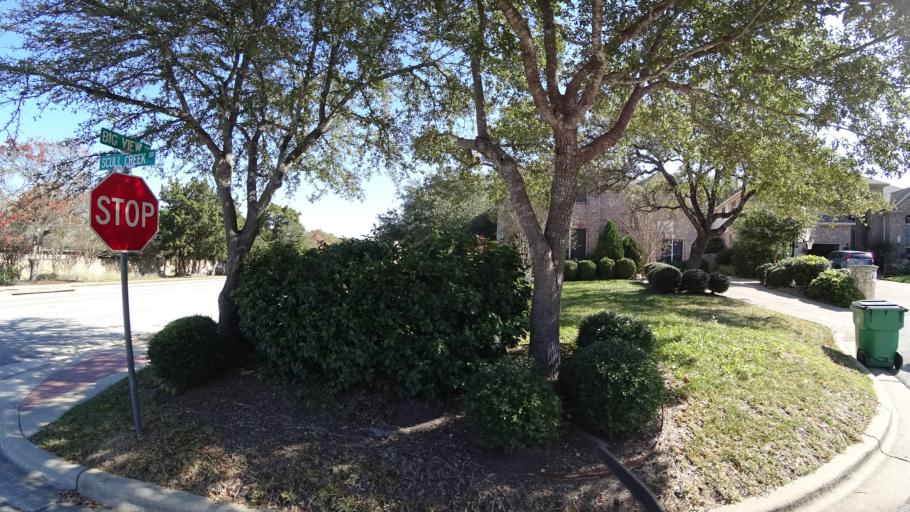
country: US
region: Texas
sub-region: Travis County
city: Lost Creek
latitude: 30.3763
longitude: -97.8483
